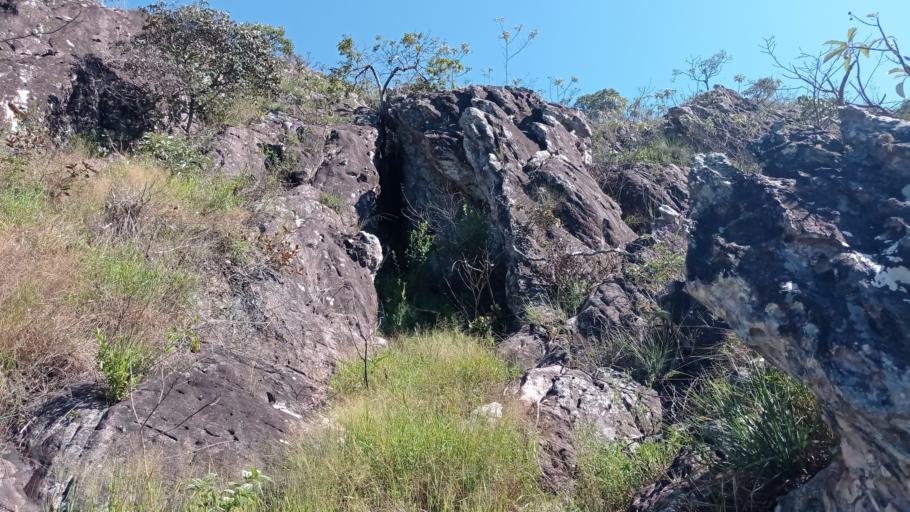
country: BR
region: Minas Gerais
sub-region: Sao Joao Del Rei
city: Sao Joao del Rei
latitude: -21.1372
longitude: -44.2866
